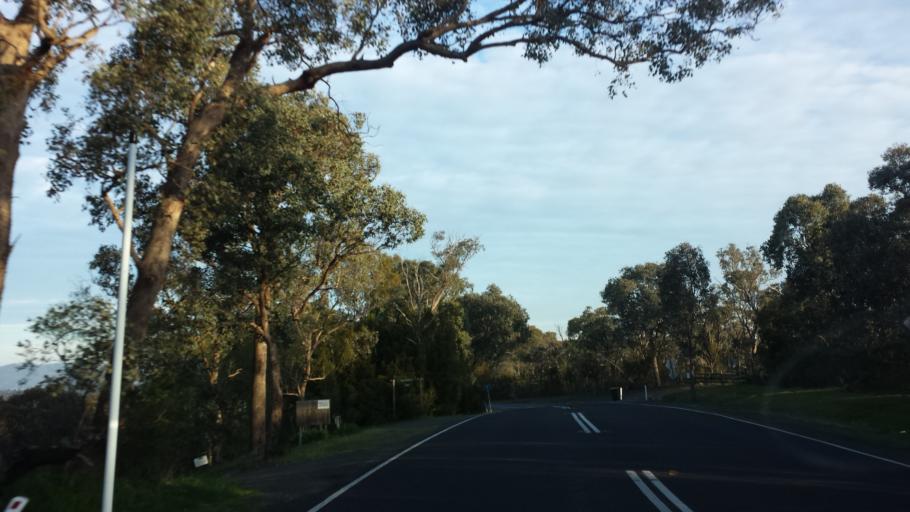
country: AU
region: Victoria
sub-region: Nillumbik
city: North Warrandyte
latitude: -37.7023
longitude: 145.2268
